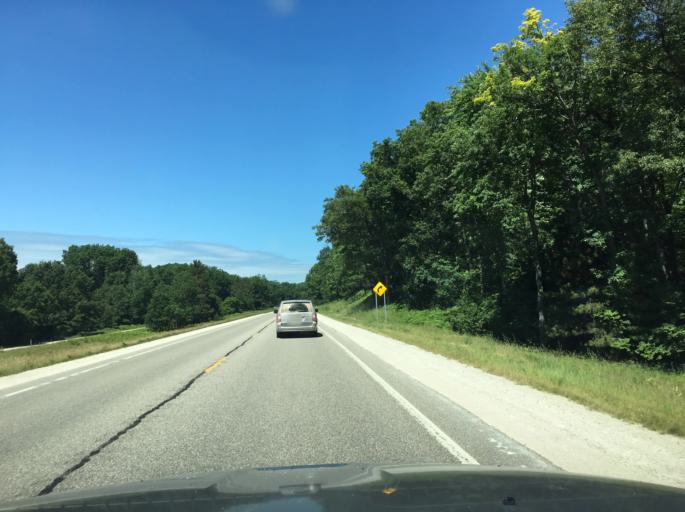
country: US
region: Michigan
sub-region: Osceola County
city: Reed City
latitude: 43.8928
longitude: -85.6755
